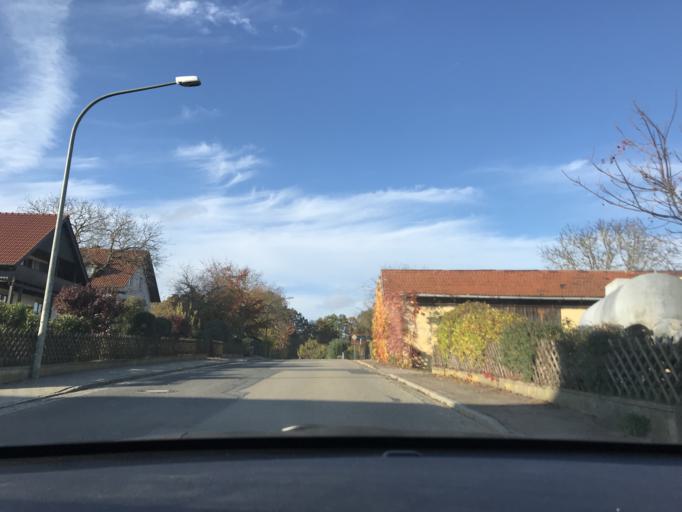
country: DE
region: Bavaria
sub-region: Upper Palatinate
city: Pentling
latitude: 48.9603
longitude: 12.0801
